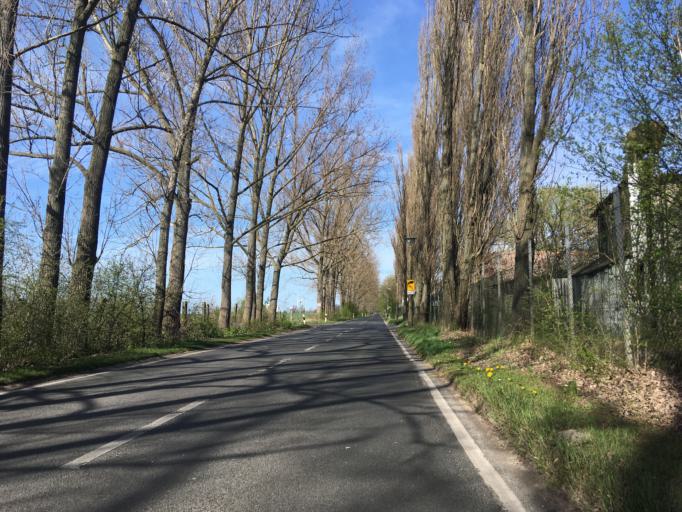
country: DE
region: Berlin
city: Wartenberg
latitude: 52.5832
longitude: 13.5223
